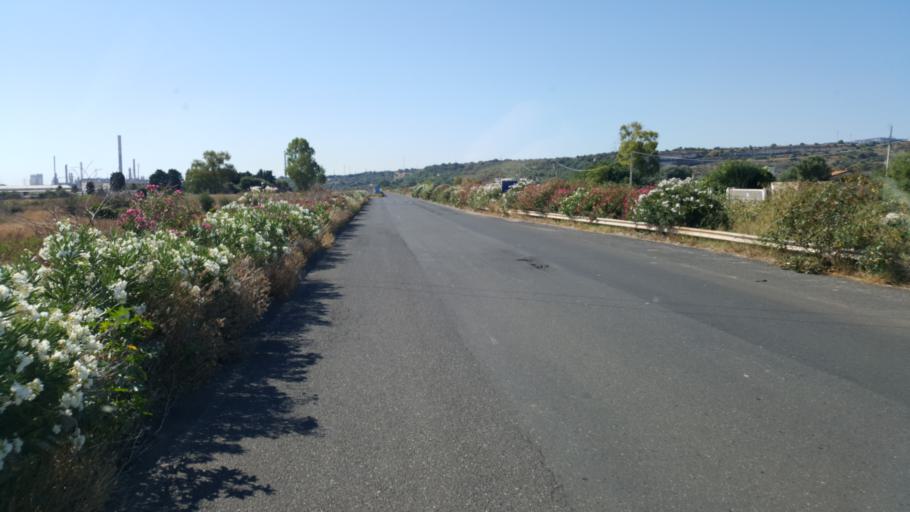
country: IT
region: Sicily
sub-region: Provincia di Siracusa
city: Melilli
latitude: 37.2010
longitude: 15.1622
